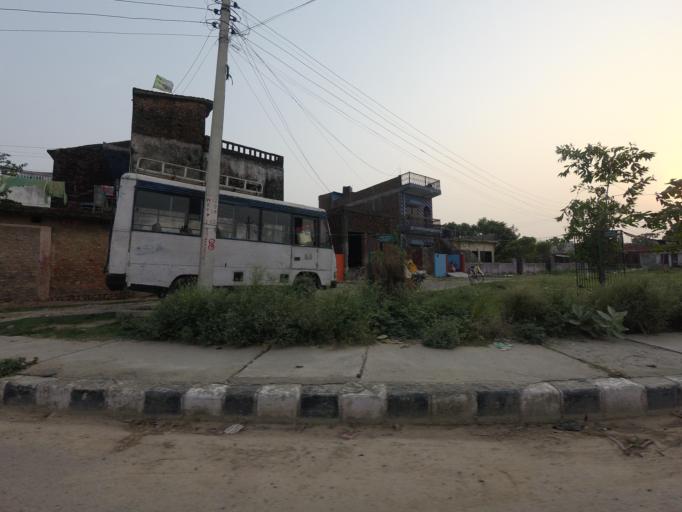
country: NP
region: Western Region
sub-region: Lumbini Zone
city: Bhairahawa
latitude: 27.5091
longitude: 83.4640
